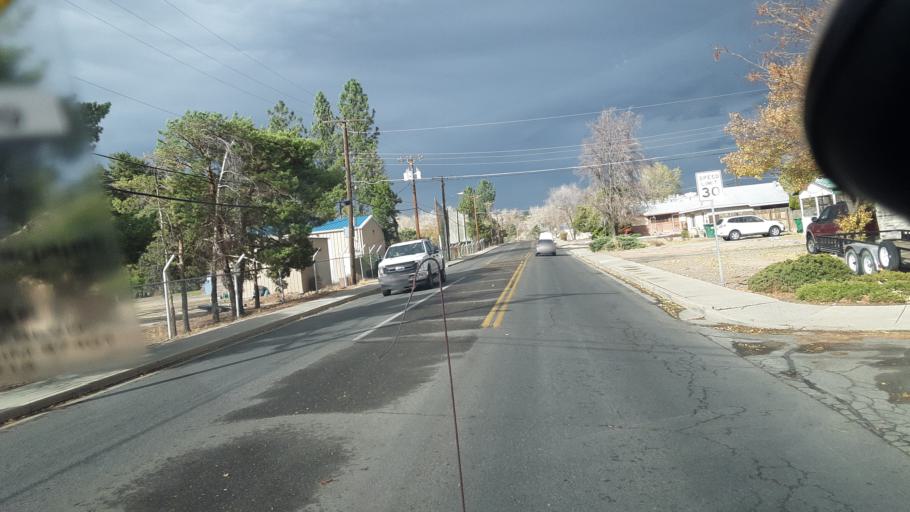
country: US
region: New Mexico
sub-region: San Juan County
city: Farmington
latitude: 36.7494
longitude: -108.1977
